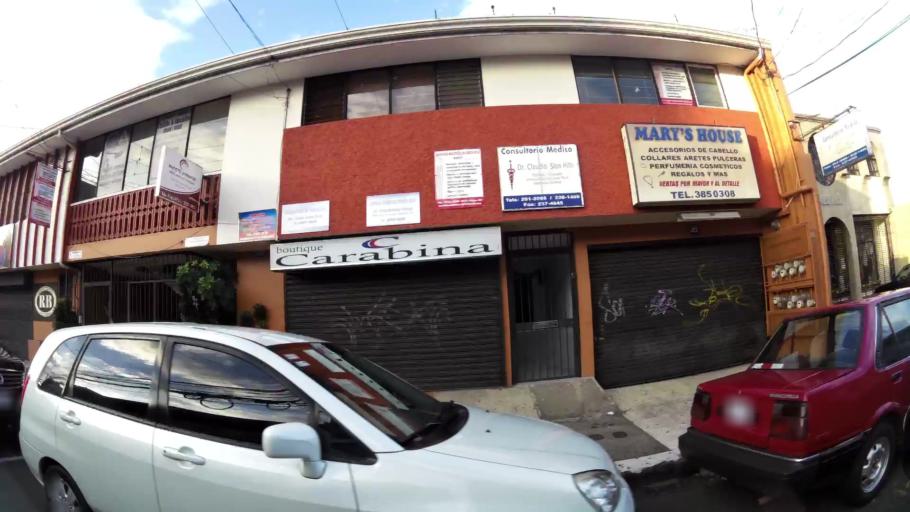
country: CR
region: Heredia
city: Heredia
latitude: 9.9979
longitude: -84.1157
